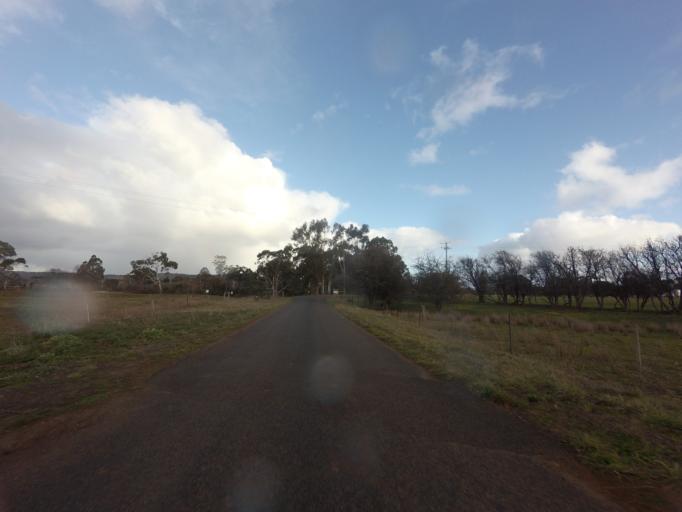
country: AU
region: Tasmania
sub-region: Break O'Day
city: St Helens
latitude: -42.0060
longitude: 148.0749
